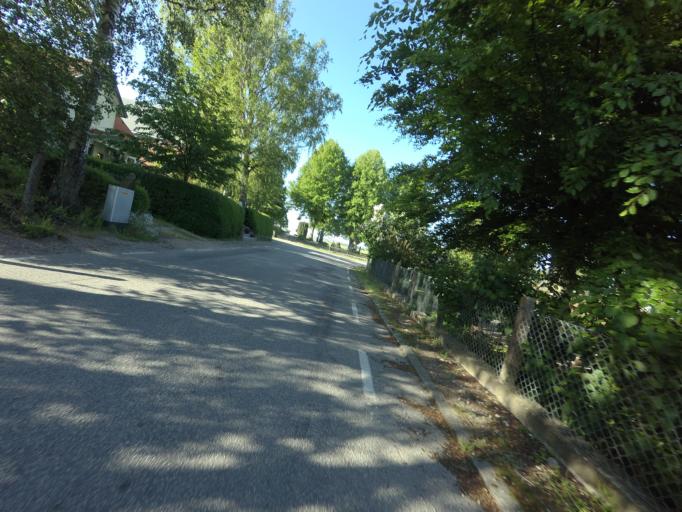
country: SE
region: Skane
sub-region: Vellinge Kommun
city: Vellinge
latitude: 55.4480
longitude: 13.0840
